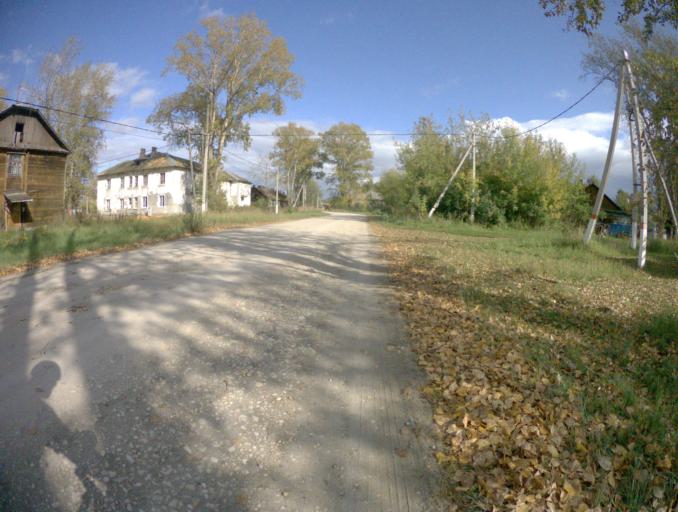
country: RU
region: Moskovskaya
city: Kerva
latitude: 55.7076
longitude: 39.5897
